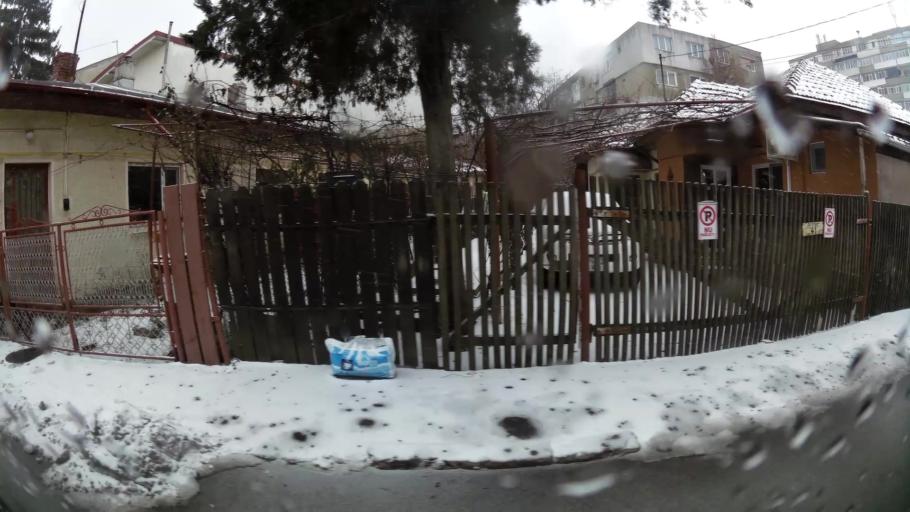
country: RO
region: Prahova
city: Ploiesti
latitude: 44.9445
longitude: 26.0017
